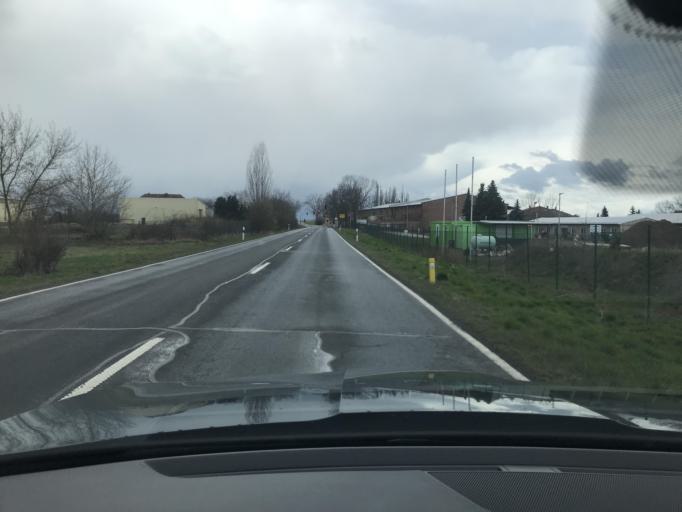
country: DE
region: Saxony-Anhalt
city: Ditfurt
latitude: 51.7878
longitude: 11.2079
